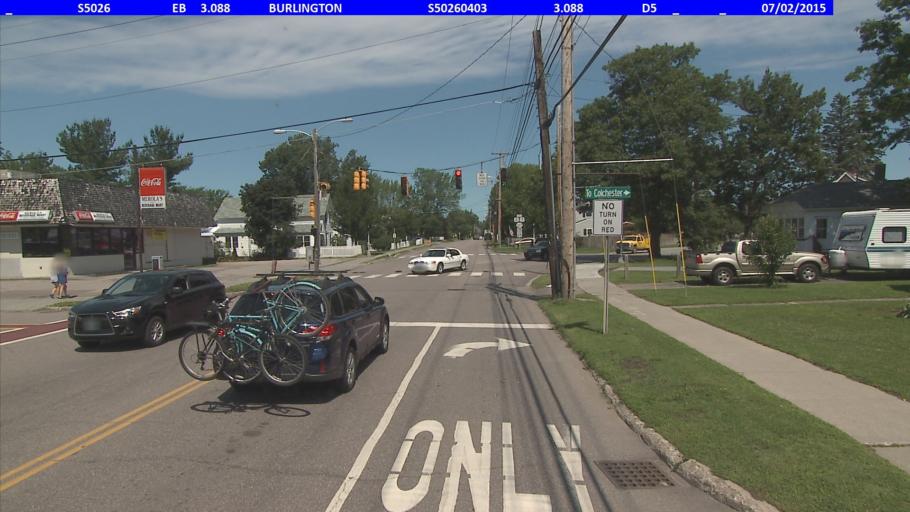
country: US
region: Vermont
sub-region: Chittenden County
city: Burlington
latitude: 44.5156
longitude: -73.2565
